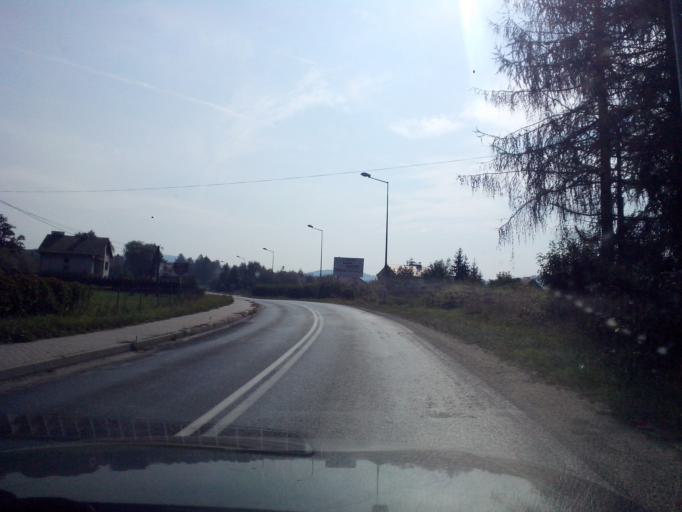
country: PL
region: Subcarpathian Voivodeship
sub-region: Powiat strzyzowski
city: Czudec
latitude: 49.9390
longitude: 21.8475
